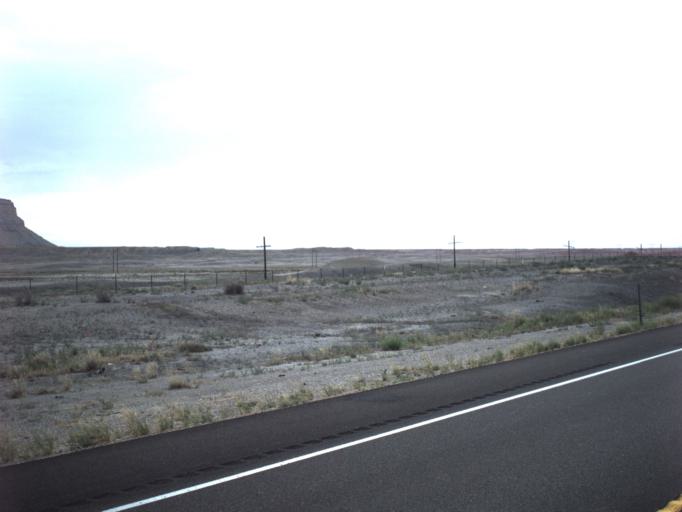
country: US
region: Utah
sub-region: Carbon County
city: East Carbon City
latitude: 39.0880
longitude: -110.3198
